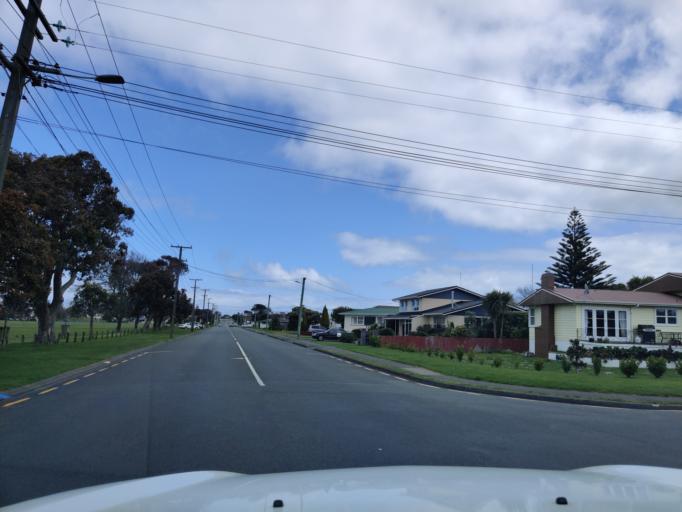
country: NZ
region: Manawatu-Wanganui
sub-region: Wanganui District
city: Wanganui
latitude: -39.9282
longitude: 175.0284
